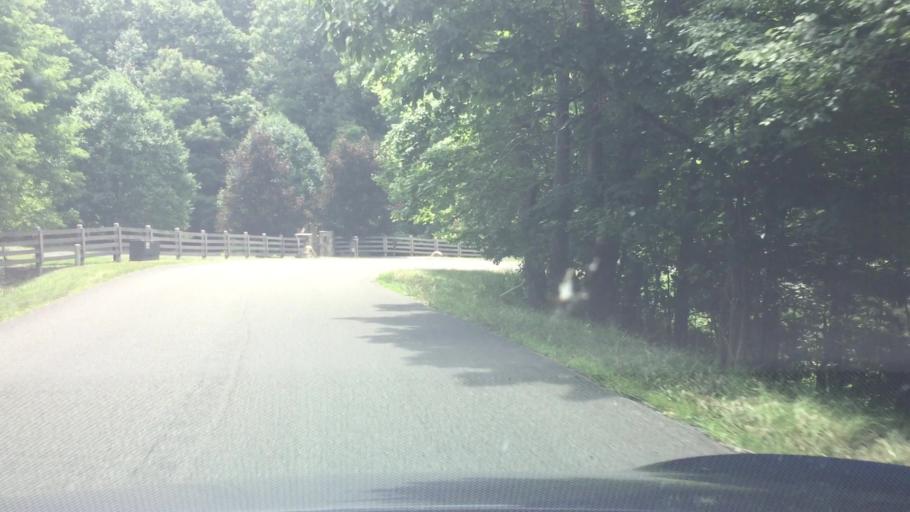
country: US
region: Virginia
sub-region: Wythe County
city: Wytheville
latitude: 36.9247
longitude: -81.0501
